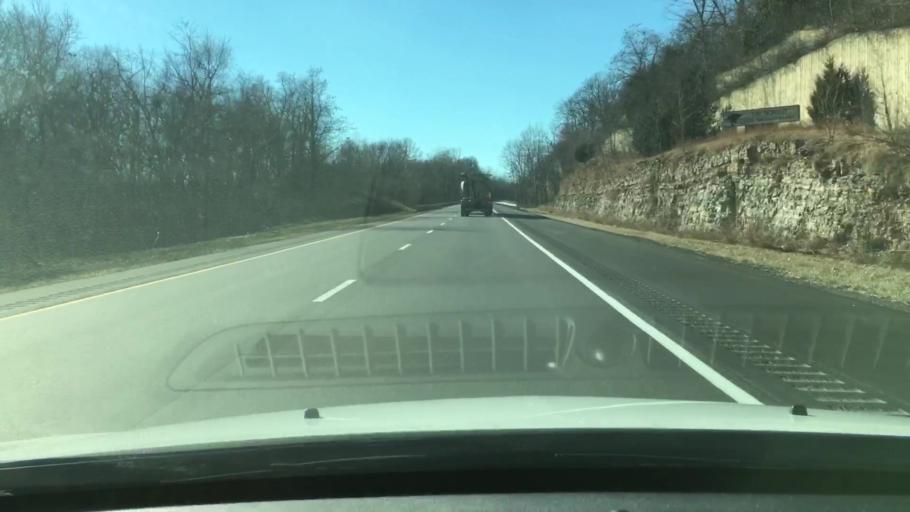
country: US
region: Illinois
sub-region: Pike County
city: Griggsville
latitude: 39.6859
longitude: -90.6489
